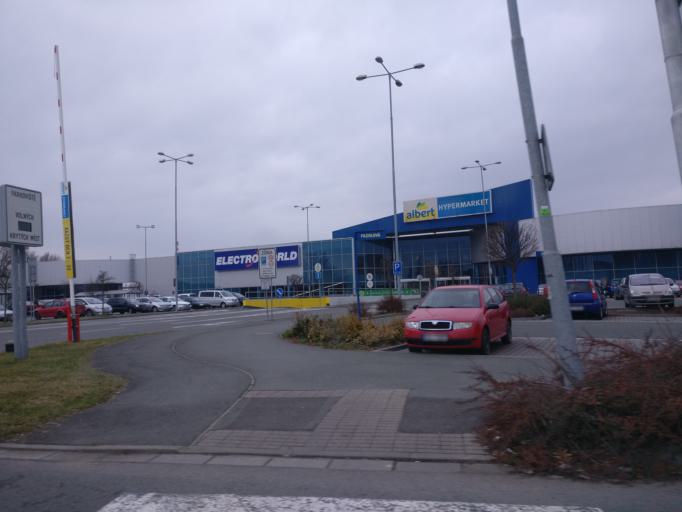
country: CZ
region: Pardubicky
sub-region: Okres Pardubice
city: Pardubice
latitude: 50.0347
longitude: 15.7547
